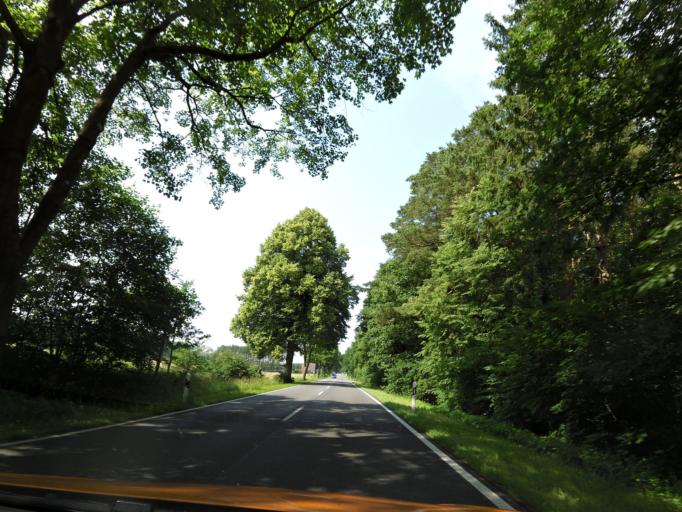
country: DE
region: Mecklenburg-Vorpommern
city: Muhl Rosin
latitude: 53.7686
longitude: 12.2452
